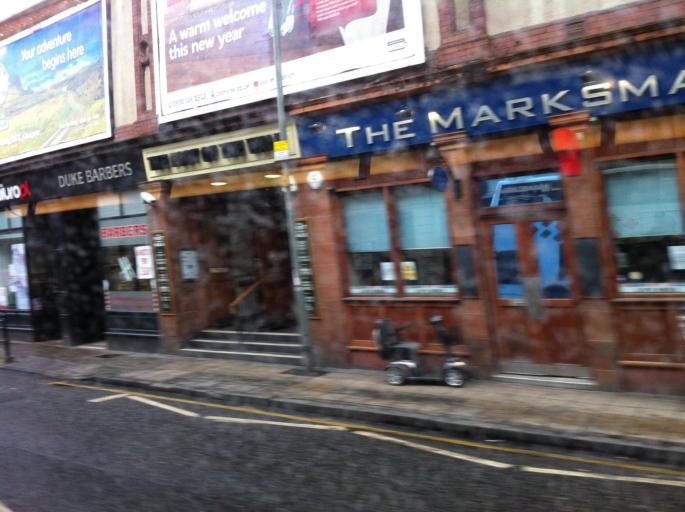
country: GB
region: Scotland
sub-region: West Lothian
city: Seafield
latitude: 55.9703
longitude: -3.1706
